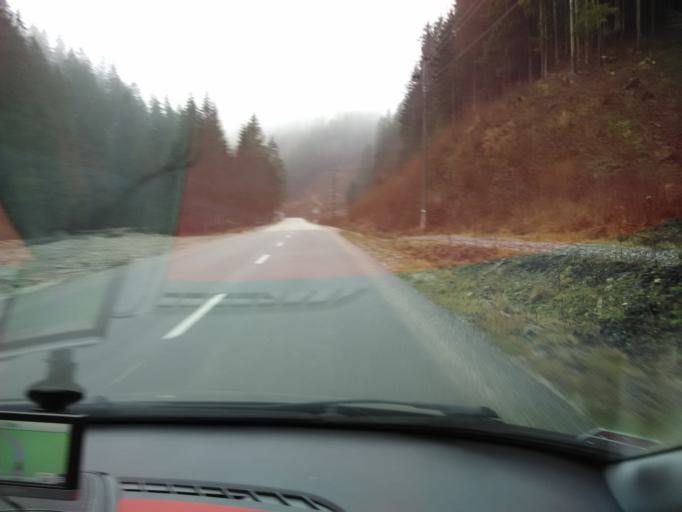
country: SK
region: Zilinsky
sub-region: Okres Zilina
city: Terchova
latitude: 49.2269
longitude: 19.0339
